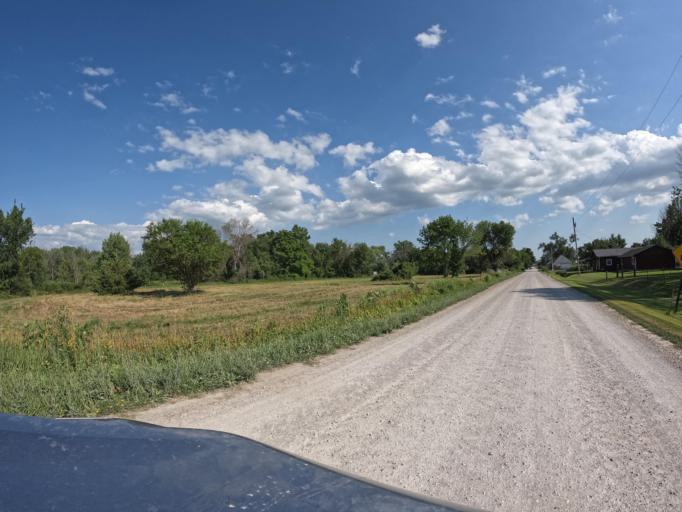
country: US
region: Iowa
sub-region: Appanoose County
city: Centerville
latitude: 40.7201
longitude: -93.0300
